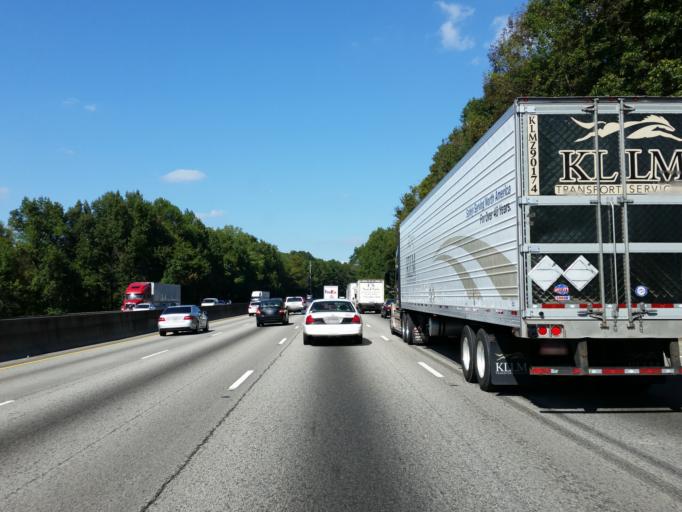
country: US
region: Georgia
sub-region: Clayton County
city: Forest Park
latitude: 33.6552
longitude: -84.3645
